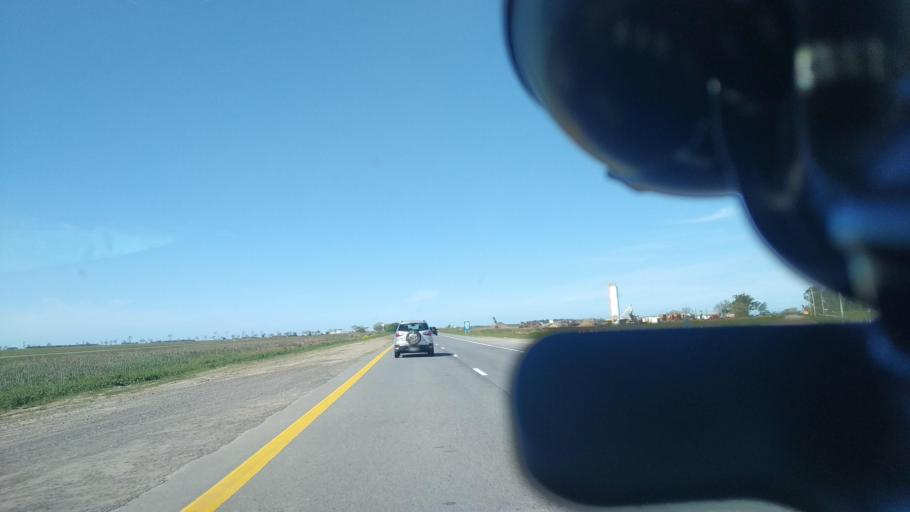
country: AR
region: Buenos Aires
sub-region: Partido de General Lavalle
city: General Lavalle
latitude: -36.4351
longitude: -56.9317
